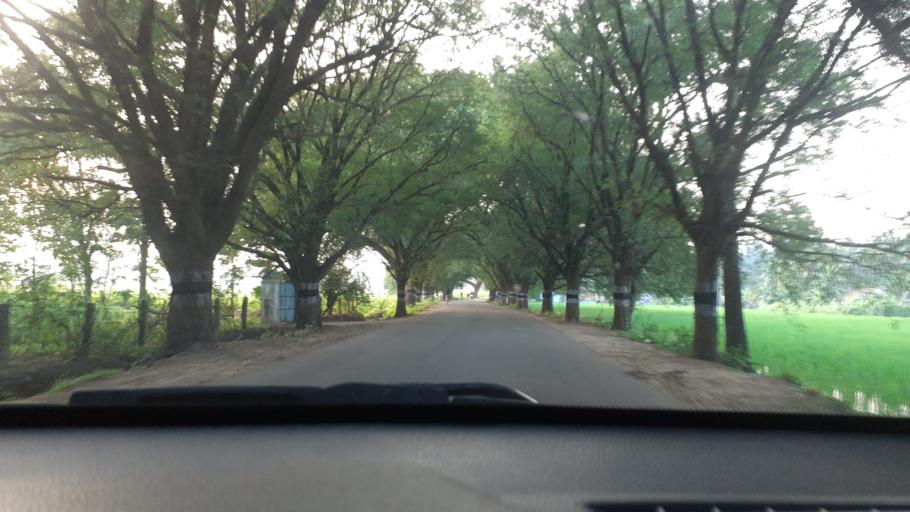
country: IN
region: Tamil Nadu
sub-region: Dindigul
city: Ayakudi
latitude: 10.4083
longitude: 77.5422
